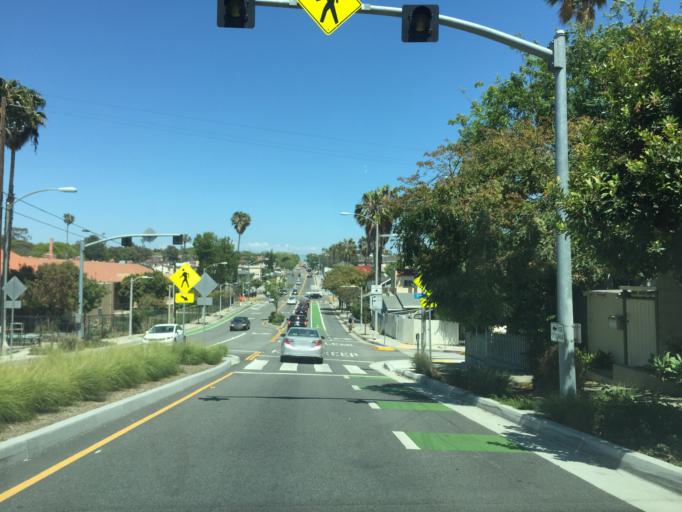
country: US
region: California
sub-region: Los Angeles County
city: Santa Monica
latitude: 34.0061
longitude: -118.4779
